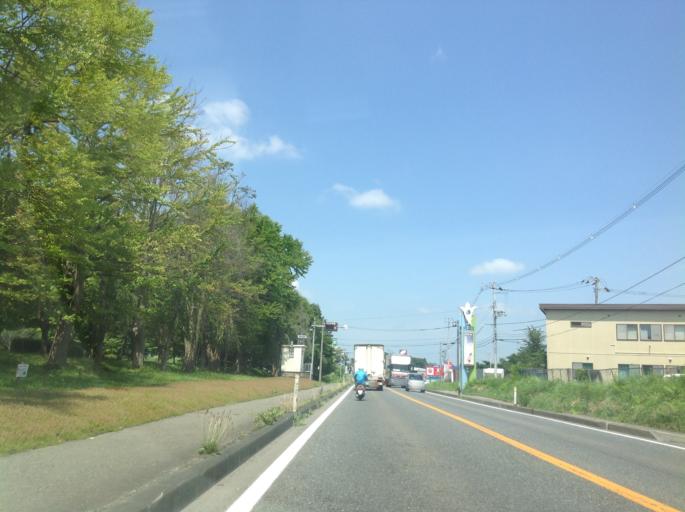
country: JP
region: Iwate
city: Hanamaki
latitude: 39.3535
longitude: 141.1104
